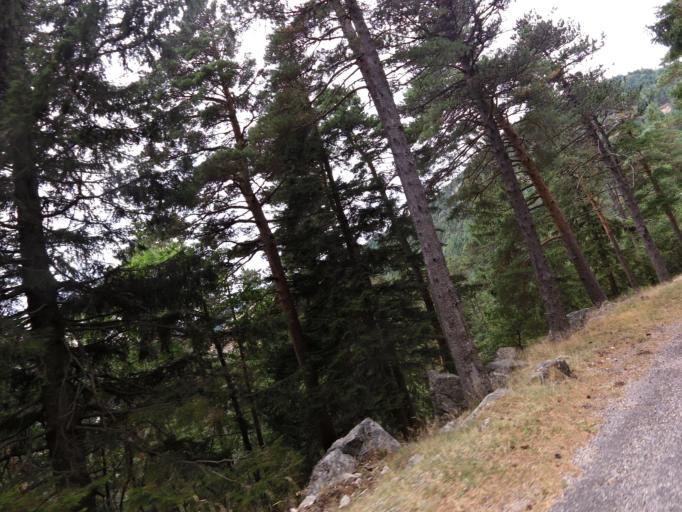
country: FR
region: Languedoc-Roussillon
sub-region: Departement du Gard
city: Valleraugue
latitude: 44.0459
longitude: 3.6078
